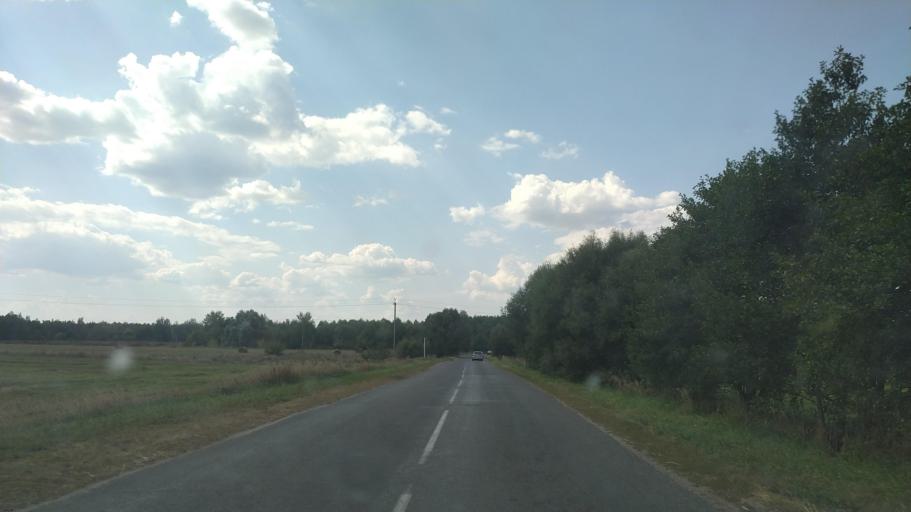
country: BY
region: Brest
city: Drahichyn
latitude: 52.1034
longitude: 25.1291
